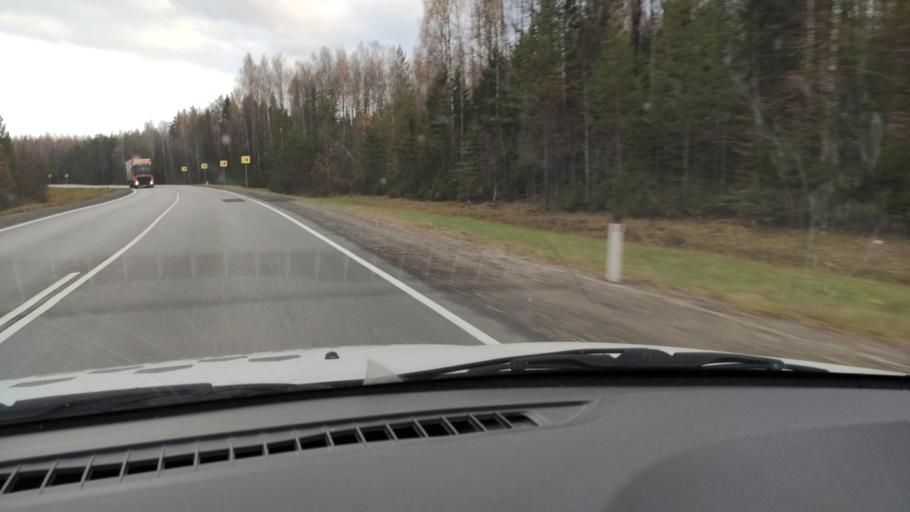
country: RU
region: Kirov
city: Chernaya Kholunitsa
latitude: 58.8325
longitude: 51.7585
